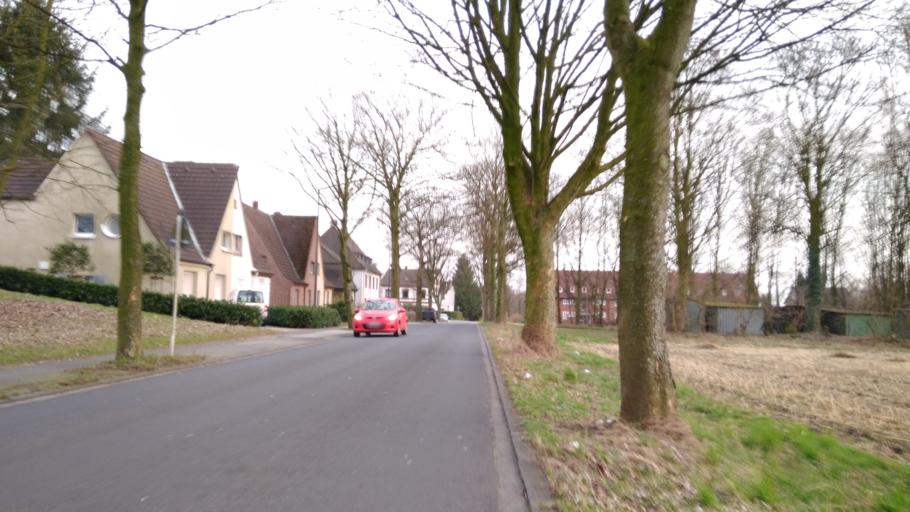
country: DE
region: North Rhine-Westphalia
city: Herten
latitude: 51.6070
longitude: 7.1139
